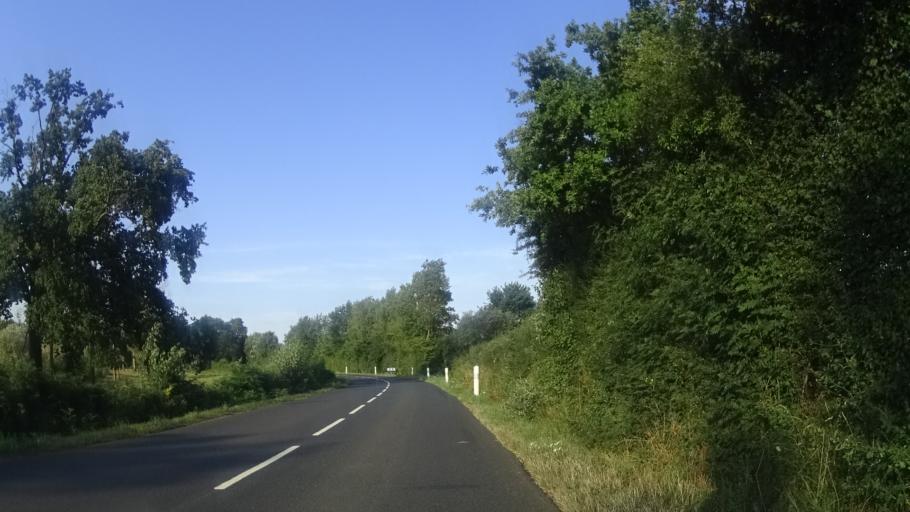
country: FR
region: Pays de la Loire
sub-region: Departement de la Loire-Atlantique
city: Riaille
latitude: 47.5210
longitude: -1.2716
